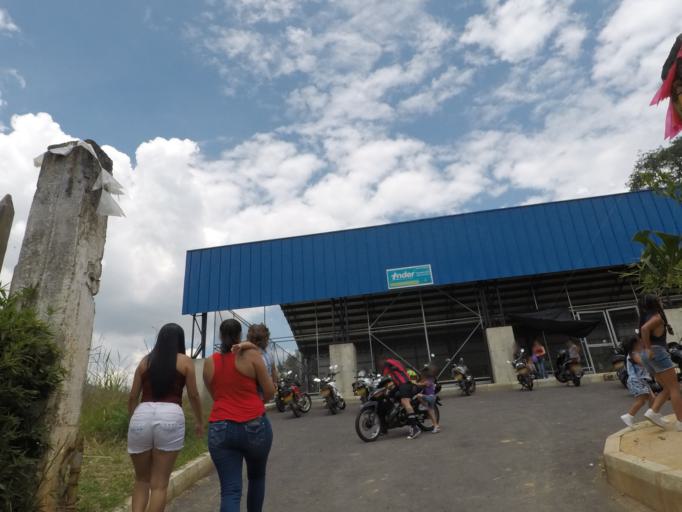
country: CO
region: Antioquia
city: Medellin
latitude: 6.2728
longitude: -75.6256
